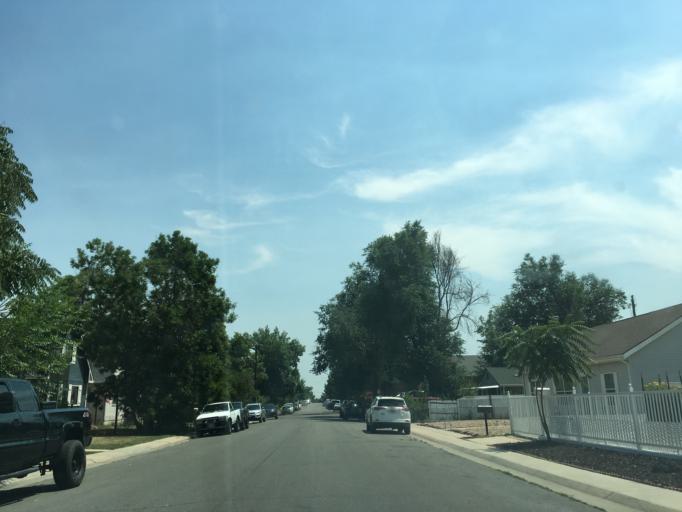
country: US
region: Colorado
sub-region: Jefferson County
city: Lakewood
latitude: 39.7022
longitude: -105.0334
